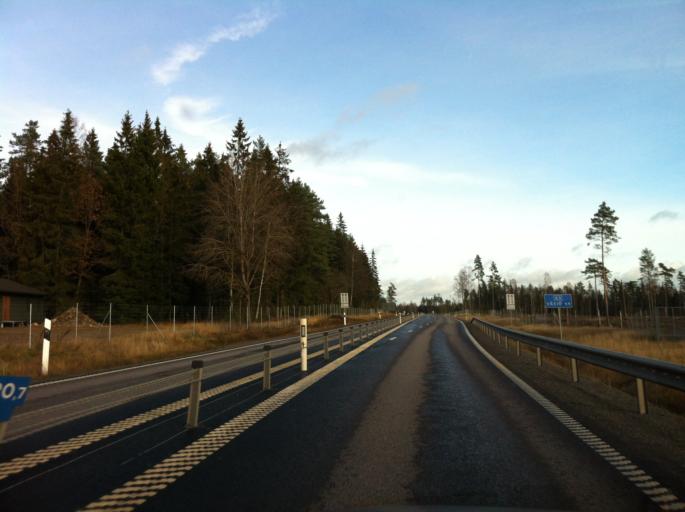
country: SE
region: Kronoberg
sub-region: Almhults Kommun
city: AElmhult
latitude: 56.6237
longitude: 14.2471
